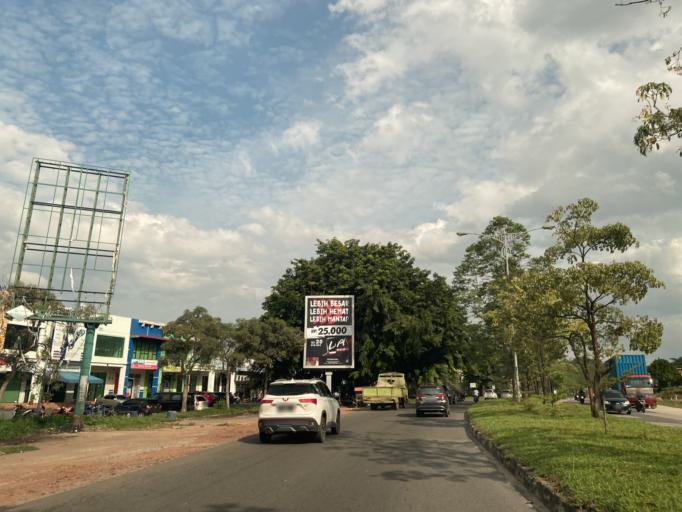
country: SG
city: Singapore
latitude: 1.1037
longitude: 104.0756
